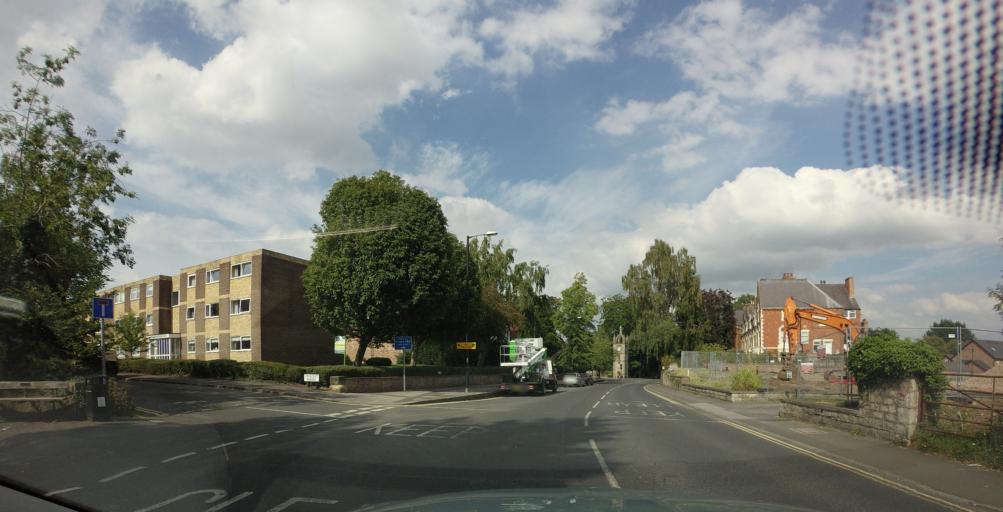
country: GB
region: England
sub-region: North Yorkshire
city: Ripon
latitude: 54.1405
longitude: -1.5238
